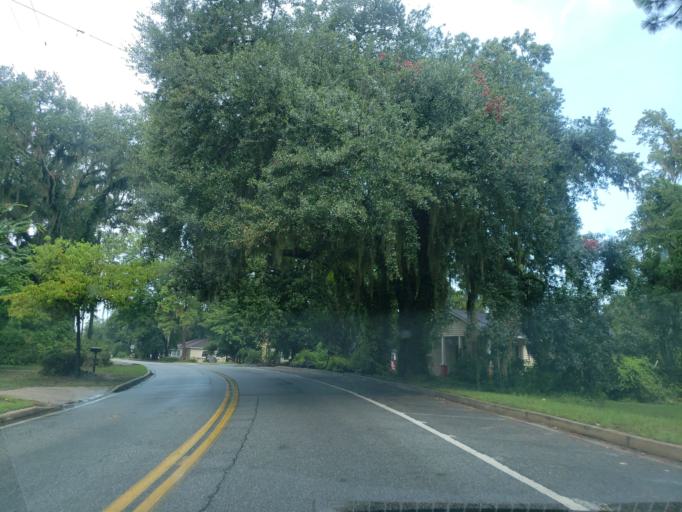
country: US
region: Georgia
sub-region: Chatham County
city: Thunderbolt
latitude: 32.0319
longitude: -81.0729
